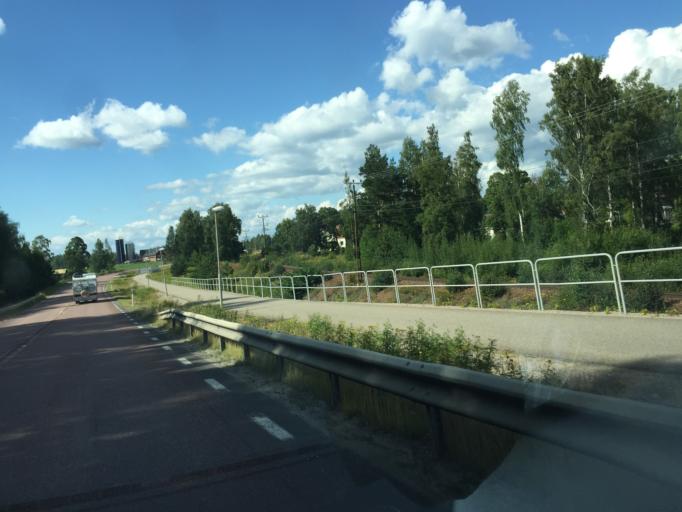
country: SE
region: Gaevleborg
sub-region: Bollnas Kommun
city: Kilafors
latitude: 61.2210
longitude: 16.5804
